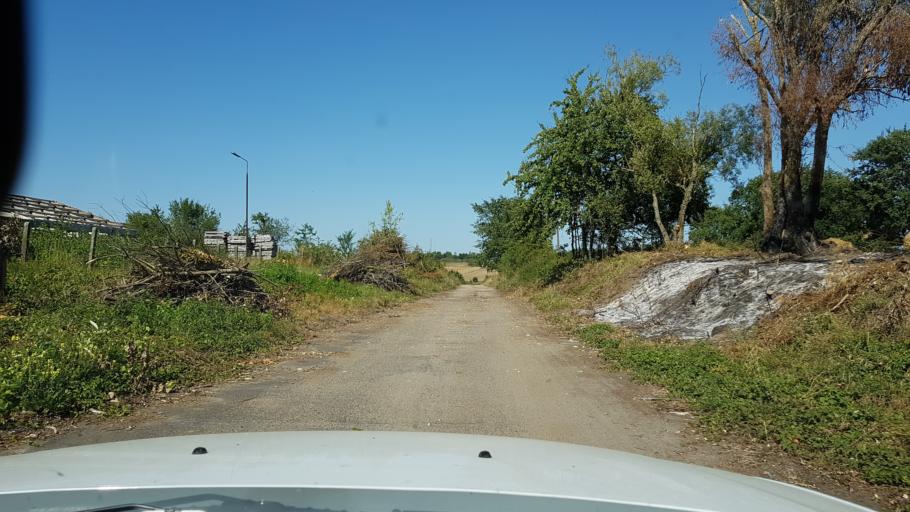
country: PL
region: West Pomeranian Voivodeship
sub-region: Powiat gryfinski
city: Moryn
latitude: 52.8447
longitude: 14.3622
